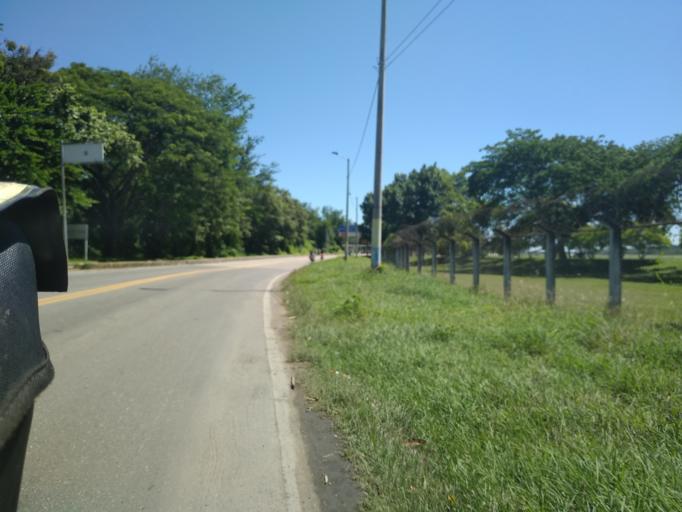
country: CO
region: Cundinamarca
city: Puerto Salgar
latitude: 5.4655
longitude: -74.6601
